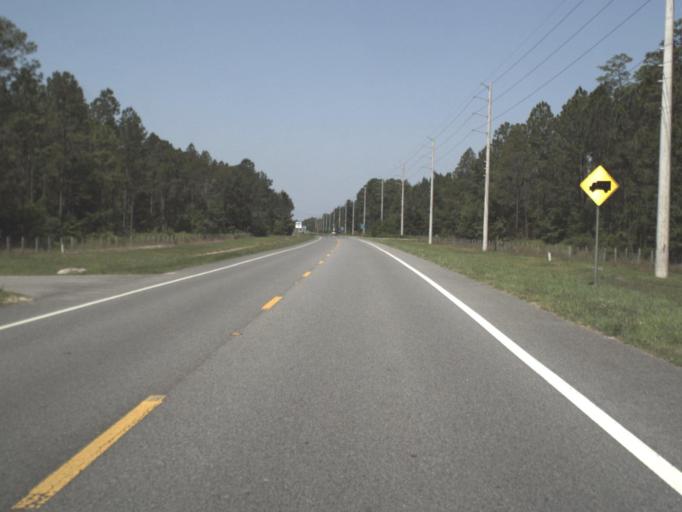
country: US
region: Florida
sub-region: Bradford County
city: Starke
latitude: 29.9568
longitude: -82.0456
